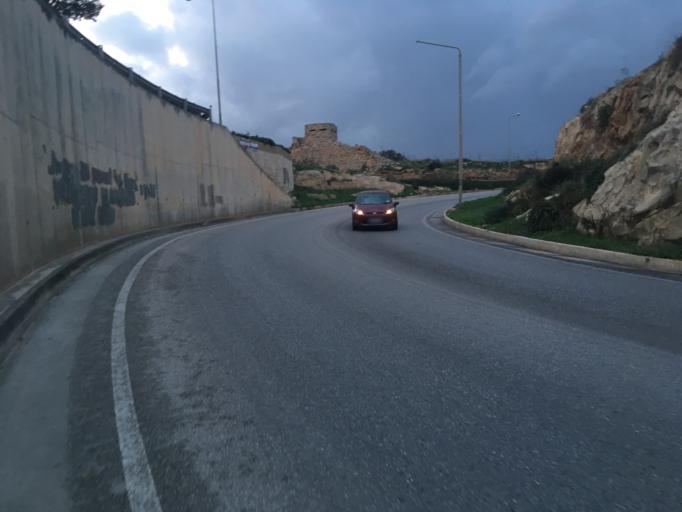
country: MT
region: Saint John
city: Saint John
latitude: 35.8997
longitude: 14.4789
